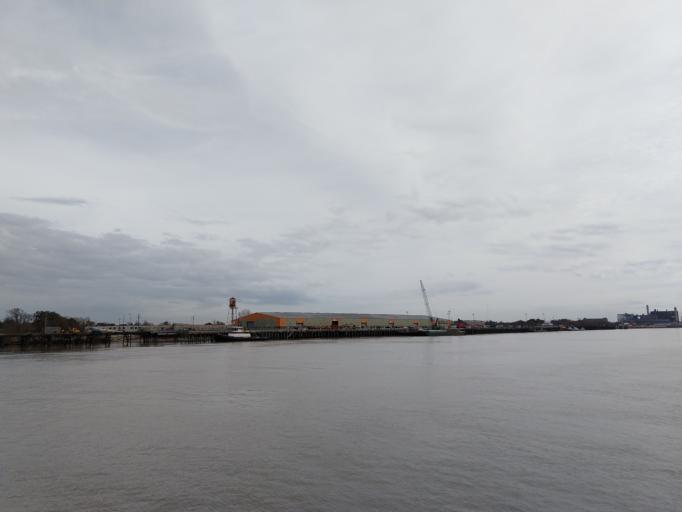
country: US
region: Louisiana
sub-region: Saint Bernard Parish
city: Arabi
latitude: 29.9523
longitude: -90.0224
